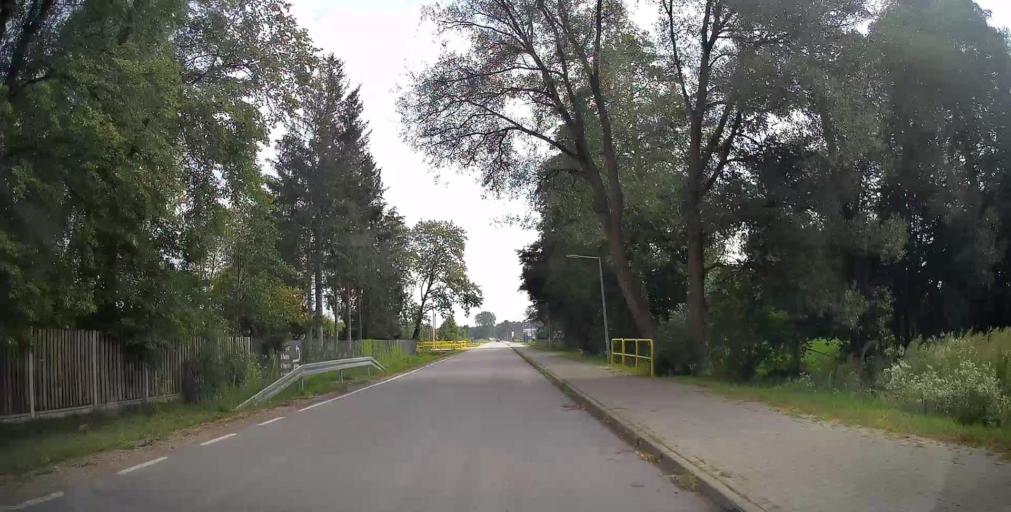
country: PL
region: Masovian Voivodeship
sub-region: Powiat bialobrzeski
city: Sucha
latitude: 51.6174
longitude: 20.9563
